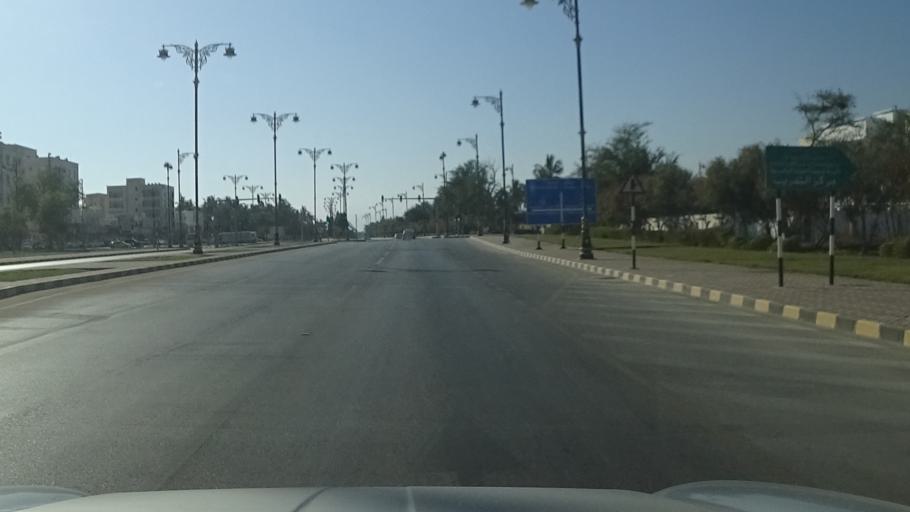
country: OM
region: Zufar
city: Salalah
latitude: 17.0262
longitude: 54.1593
